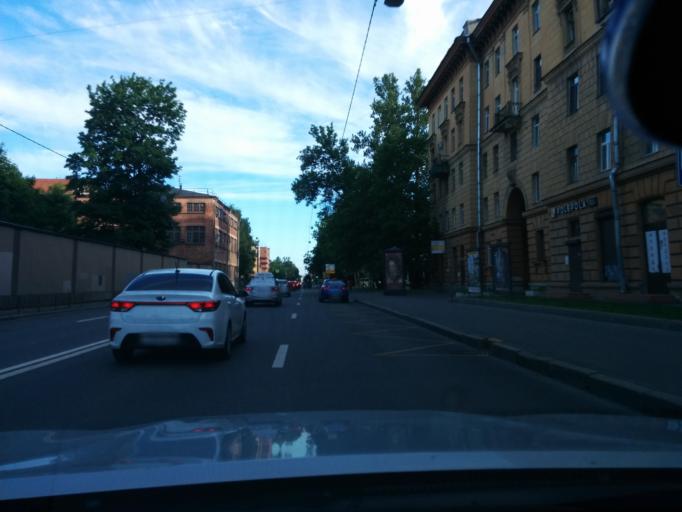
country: RU
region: Leningrad
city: Sampsonievskiy
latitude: 59.9813
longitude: 30.3365
